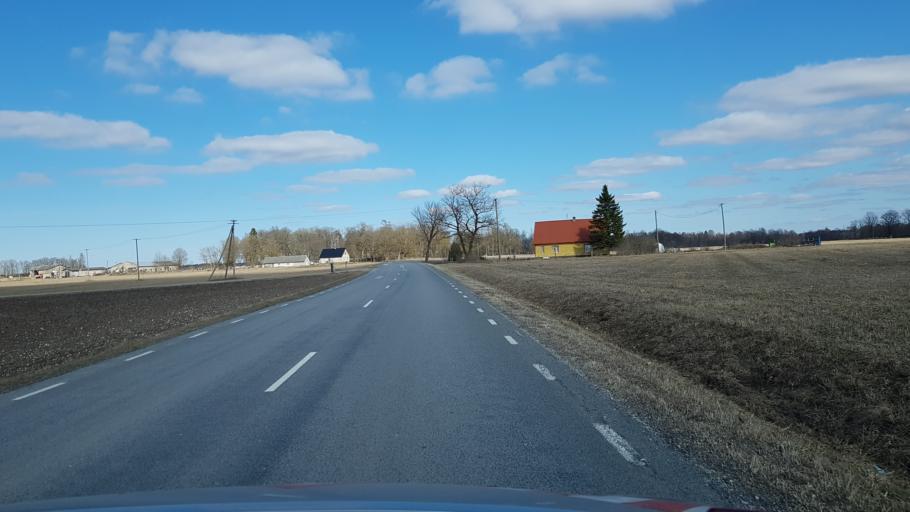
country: EE
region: Laeaene-Virumaa
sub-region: Tapa vald
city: Tapa
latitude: 59.2685
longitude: 25.8549
